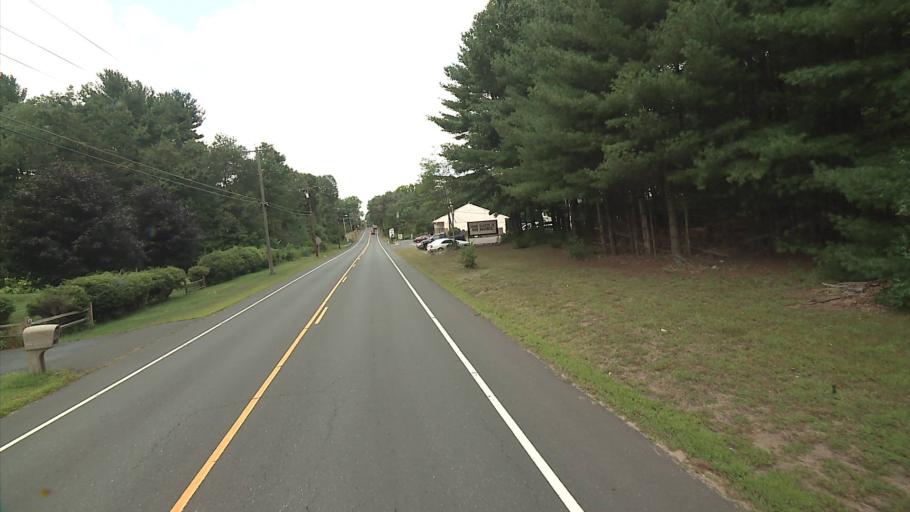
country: US
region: Connecticut
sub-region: Hartford County
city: Tariffville
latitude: 41.9341
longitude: -72.7692
